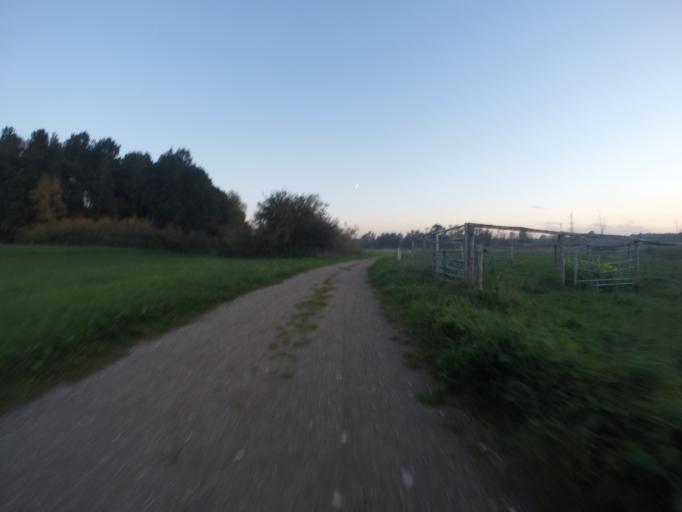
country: DK
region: Capital Region
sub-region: Hoje-Taastrup Kommune
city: Taastrup
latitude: 55.6647
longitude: 12.3211
